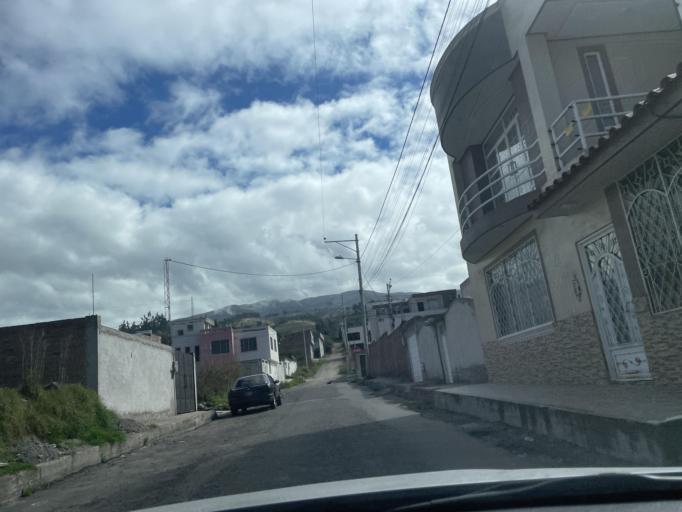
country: EC
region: Chimborazo
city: Guano
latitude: -1.6064
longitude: -78.6389
